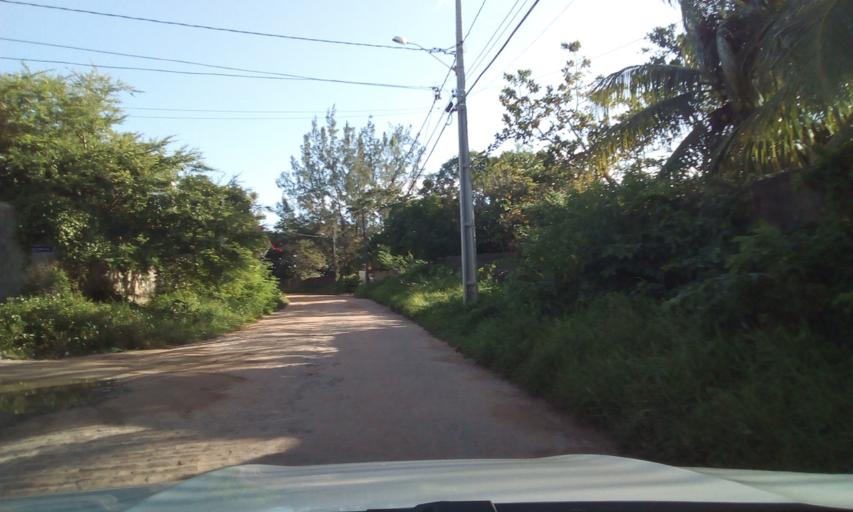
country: BR
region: Paraiba
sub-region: Joao Pessoa
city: Joao Pessoa
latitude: -7.1560
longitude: -34.8485
